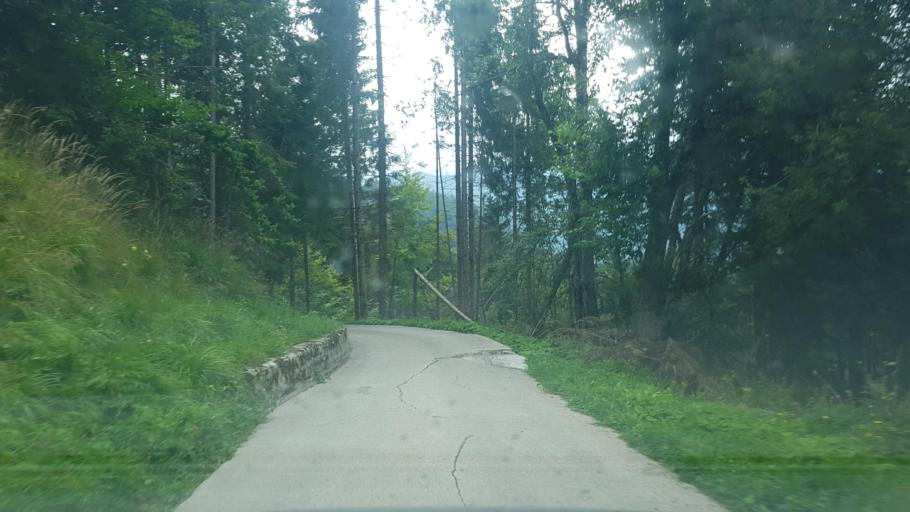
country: IT
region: Friuli Venezia Giulia
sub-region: Provincia di Udine
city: Rigolato
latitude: 46.5514
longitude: 12.8209
